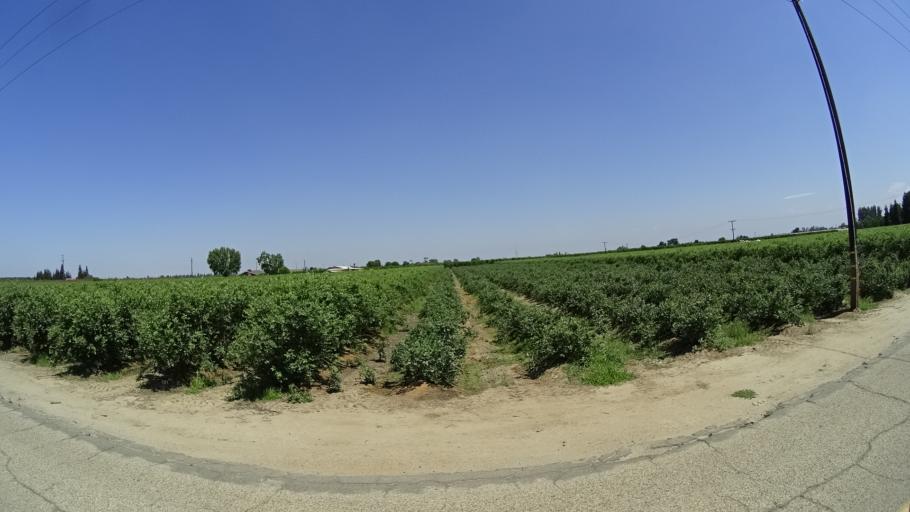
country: US
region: California
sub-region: Fresno County
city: Kingsburg
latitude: 36.4888
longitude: -119.5466
